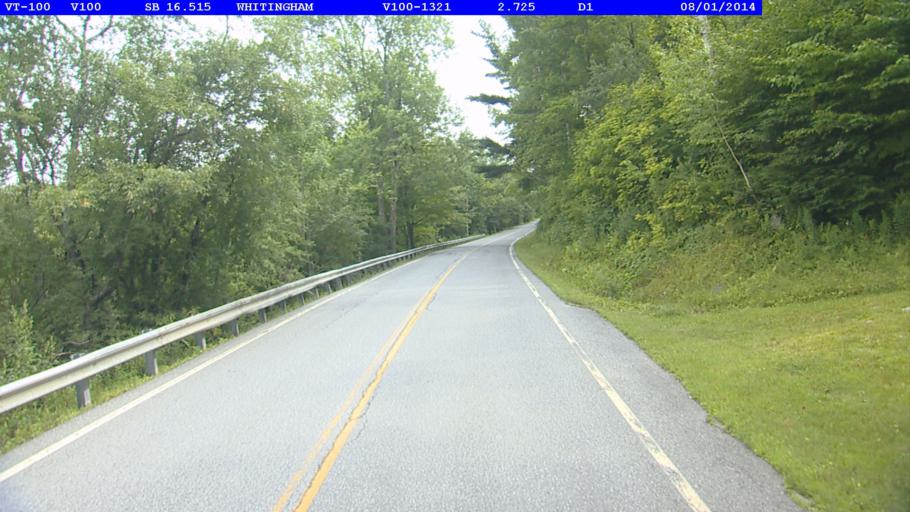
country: US
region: Massachusetts
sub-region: Franklin County
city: Charlemont
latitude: 42.7771
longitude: -72.8962
